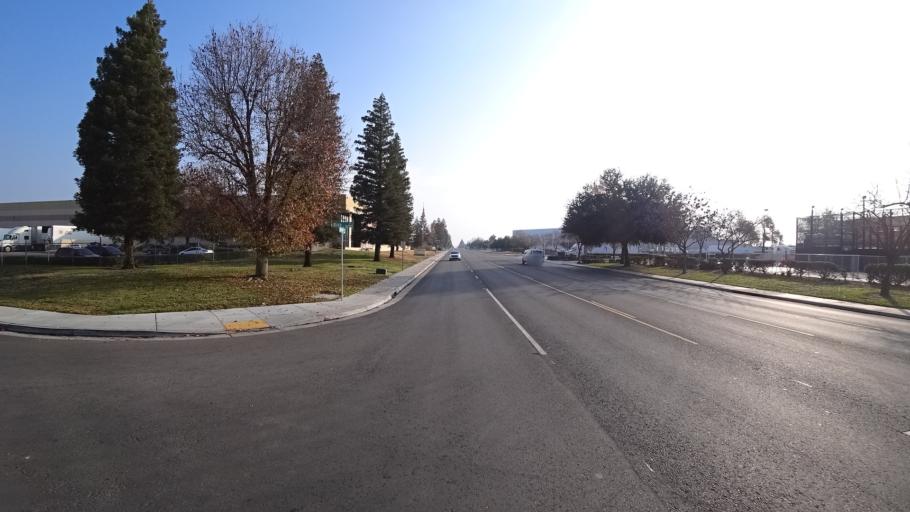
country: US
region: California
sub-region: Kern County
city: Greenacres
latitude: 35.3133
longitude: -119.0902
